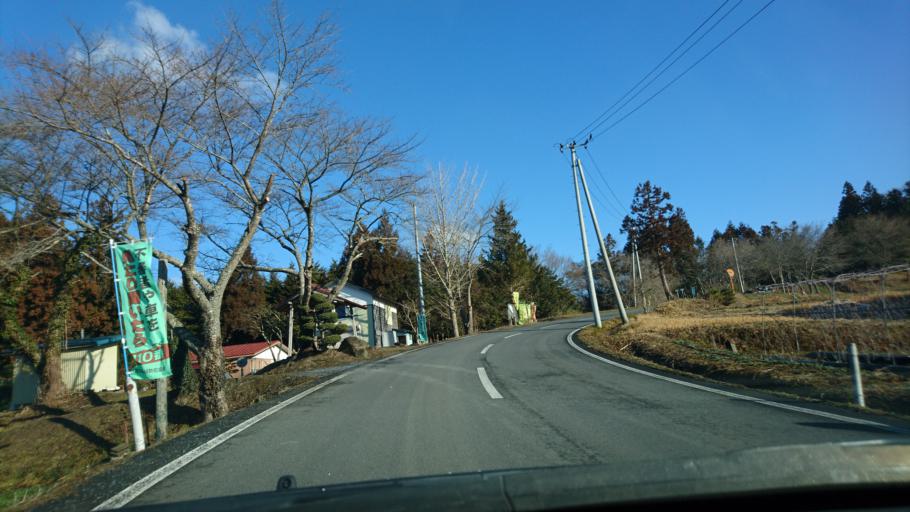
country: JP
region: Iwate
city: Ichinoseki
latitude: 38.8577
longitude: 141.2974
